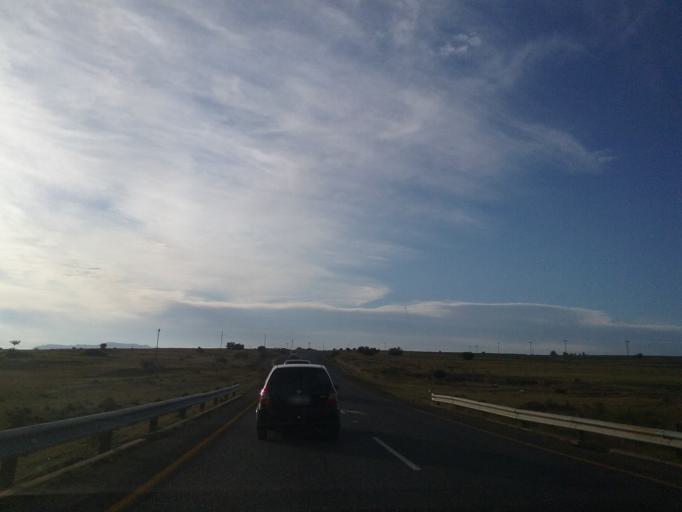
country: LS
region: Mohale's Hoek District
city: Mohale's Hoek
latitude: -30.2033
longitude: 27.4236
